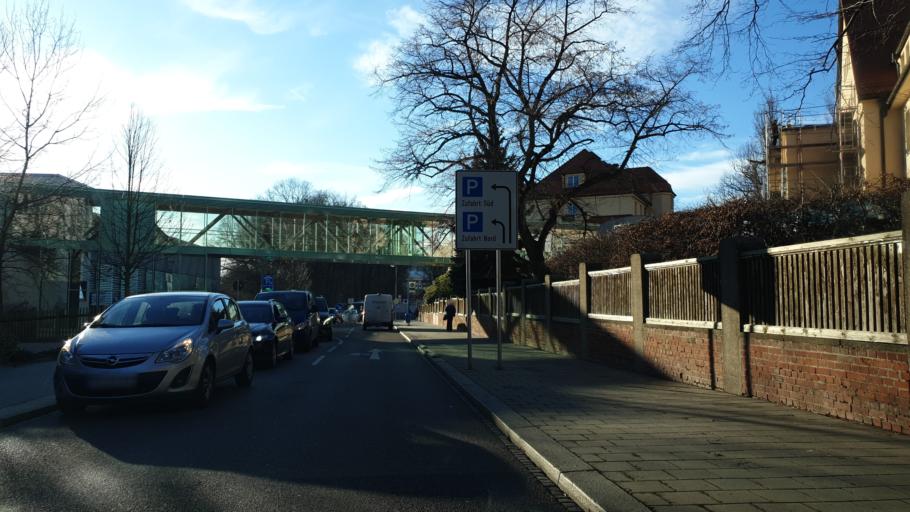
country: DE
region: Saxony
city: Chemnitz
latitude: 50.8471
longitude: 12.8951
